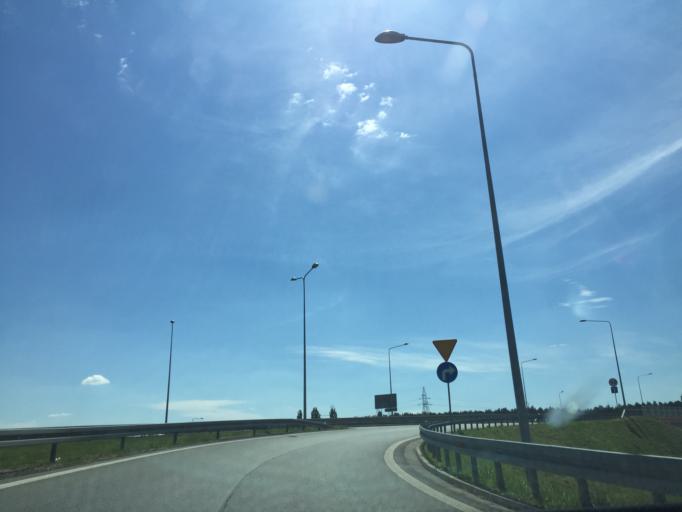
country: PL
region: Lodz Voivodeship
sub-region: Piotrkow Trybunalski
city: Piotrkow Trybunalski
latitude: 51.4444
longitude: 19.7228
